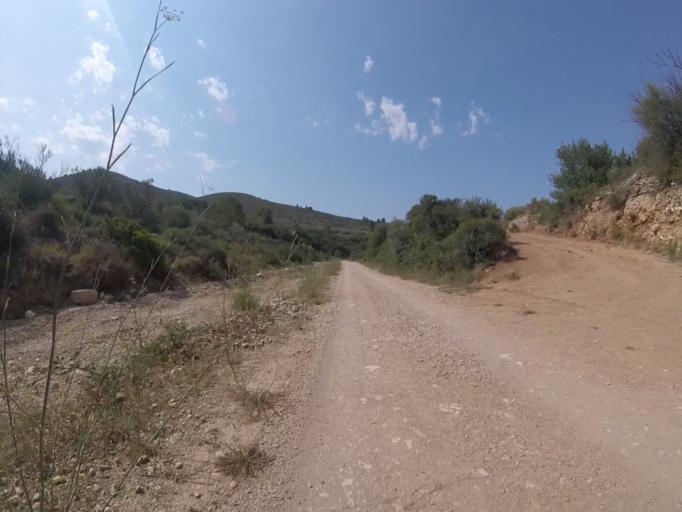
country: ES
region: Valencia
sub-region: Provincia de Castello
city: Cuevas de Vinroma
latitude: 40.3100
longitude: 0.1765
